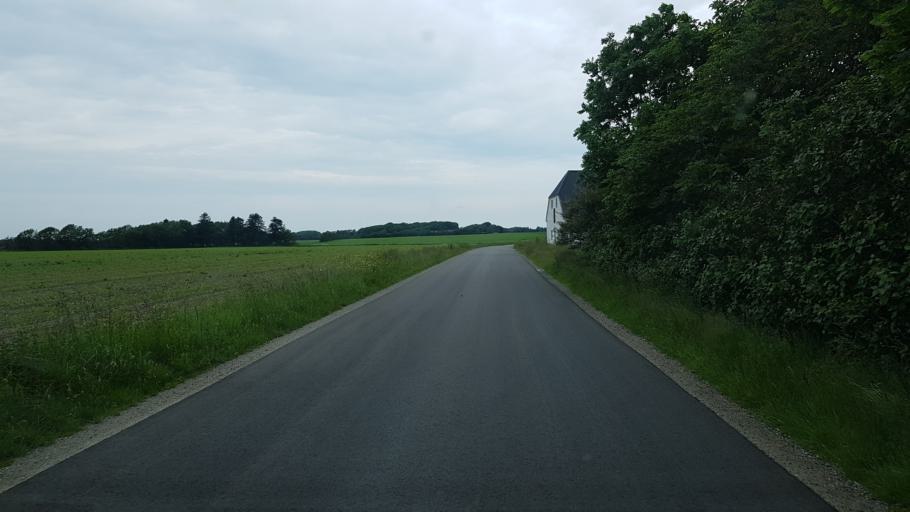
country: DK
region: South Denmark
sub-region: Varde Kommune
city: Oksbol
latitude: 55.7351
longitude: 8.3715
